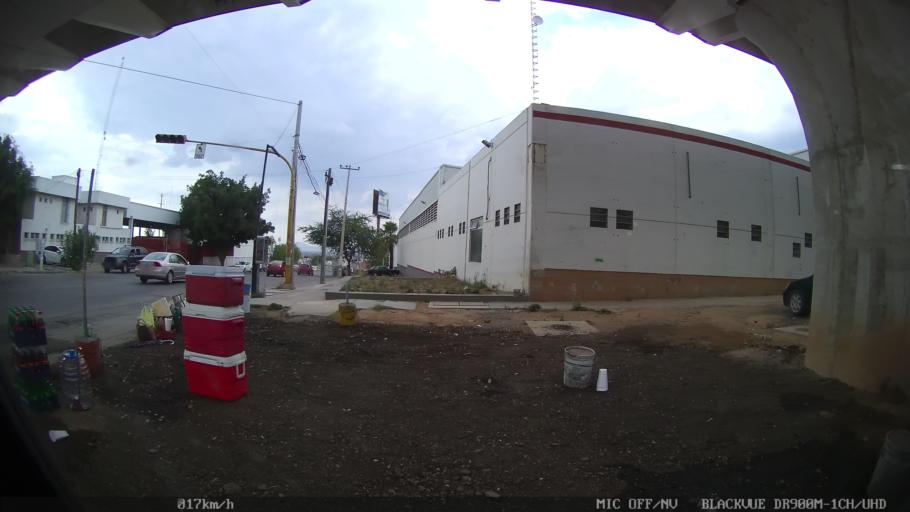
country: MX
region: Jalisco
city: Tlaquepaque
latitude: 20.6221
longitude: -103.2811
